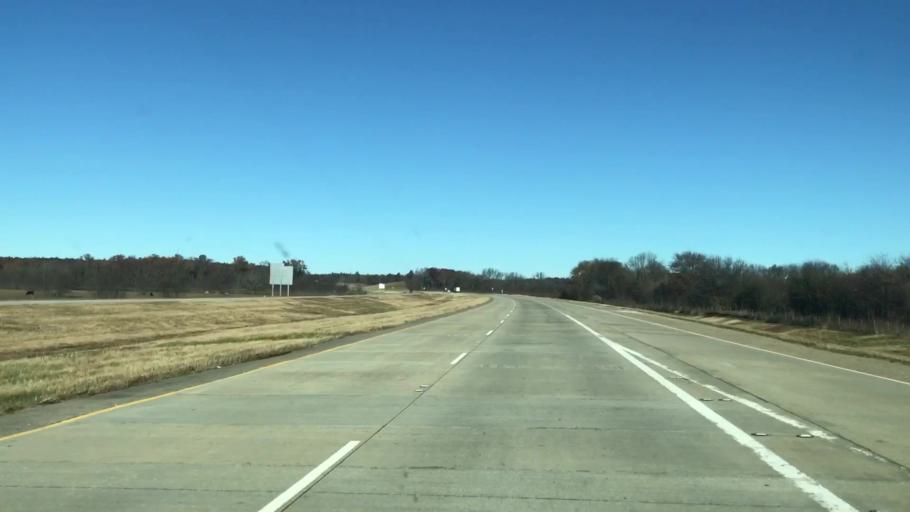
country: US
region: Louisiana
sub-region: Caddo Parish
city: Vivian
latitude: 32.9032
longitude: -93.8641
